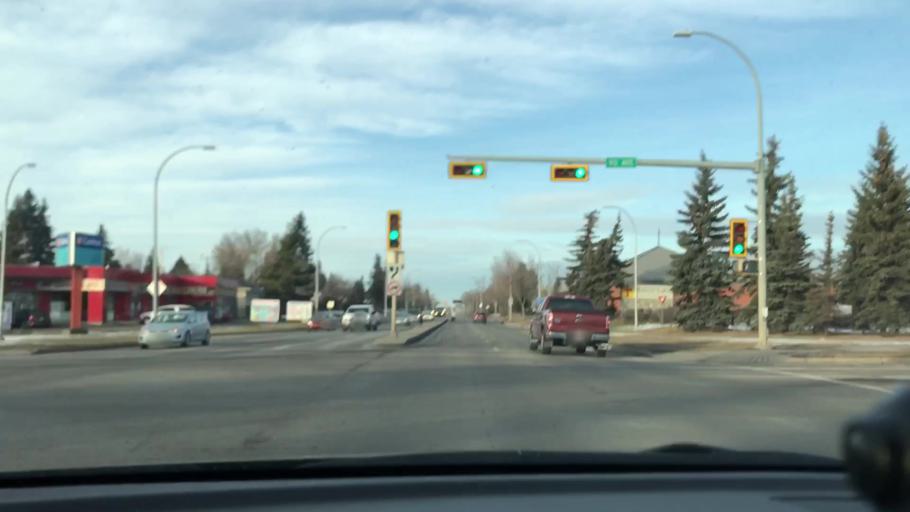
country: CA
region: Alberta
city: Edmonton
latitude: 53.5252
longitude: -113.4428
